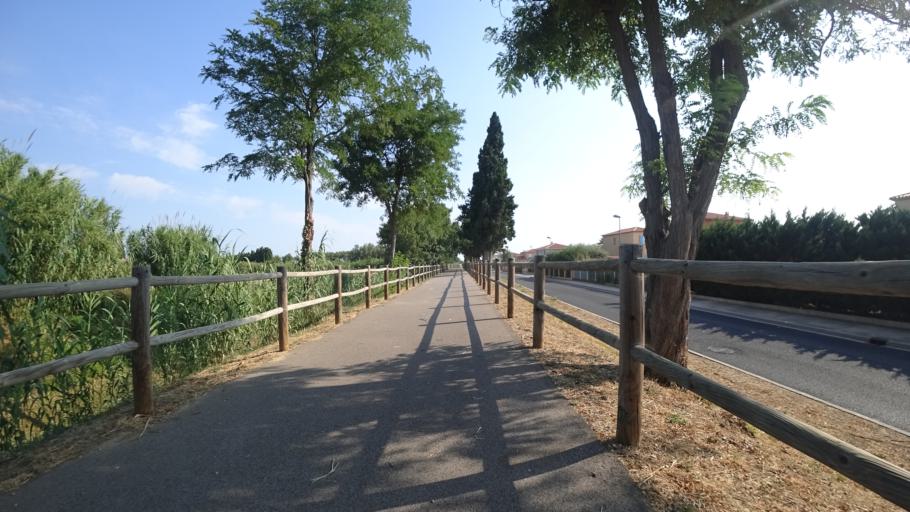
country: FR
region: Languedoc-Roussillon
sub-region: Departement des Pyrenees-Orientales
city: Saint-Laurent-de-la-Salanque
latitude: 42.7737
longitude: 2.9819
